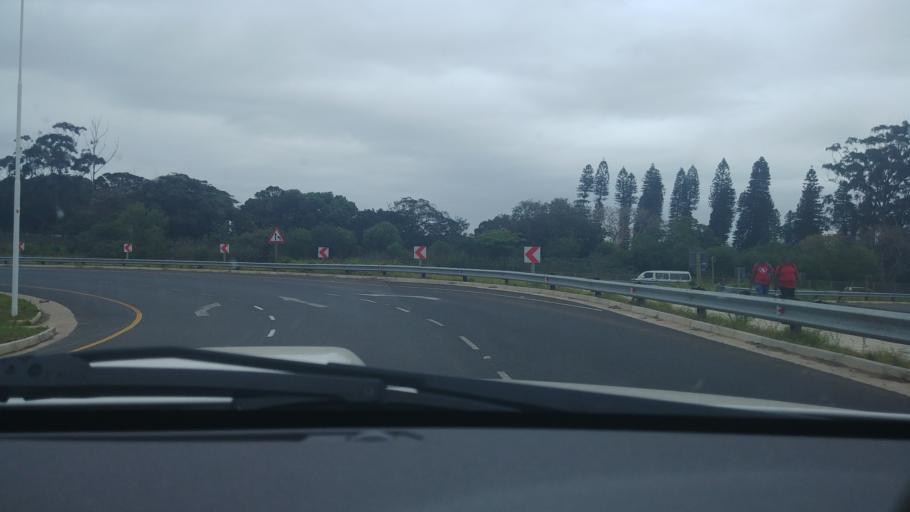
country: ZA
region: KwaZulu-Natal
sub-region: eThekwini Metropolitan Municipality
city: Durban
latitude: -29.7092
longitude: 31.0496
